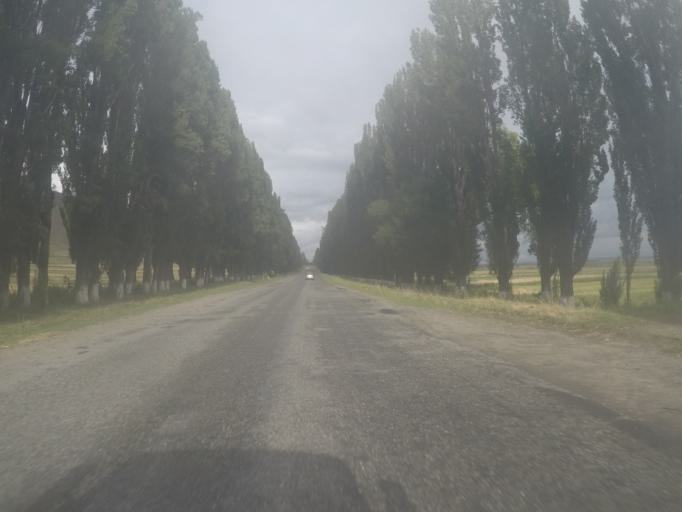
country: KG
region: Ysyk-Koel
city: Tyup
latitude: 42.7425
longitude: 78.0338
